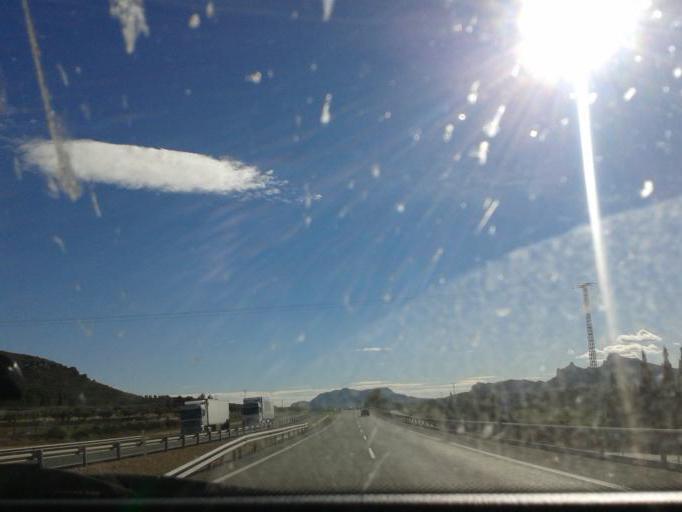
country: ES
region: Valencia
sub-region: Provincia de Alicante
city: Villena
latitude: 38.5921
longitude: -0.8445
